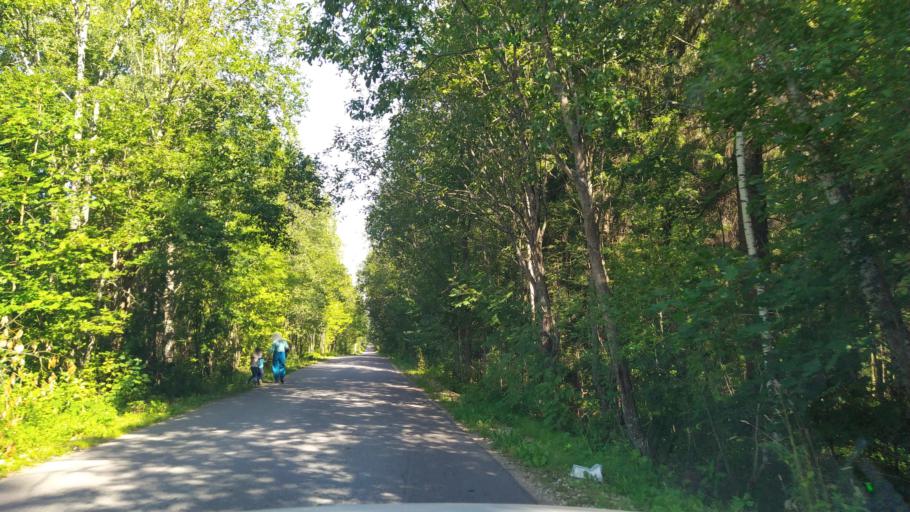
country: RU
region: Leningrad
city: Rozhdestveno
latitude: 59.2690
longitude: 30.0245
